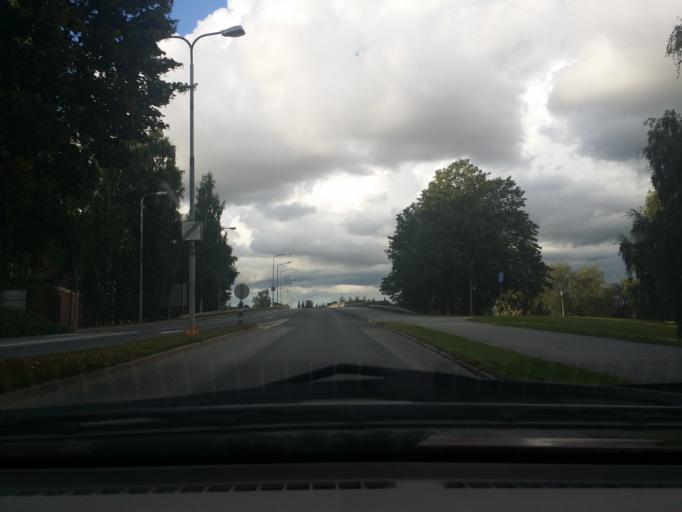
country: FI
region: Satakunta
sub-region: Pori
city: Pori
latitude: 61.4889
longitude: 21.8034
